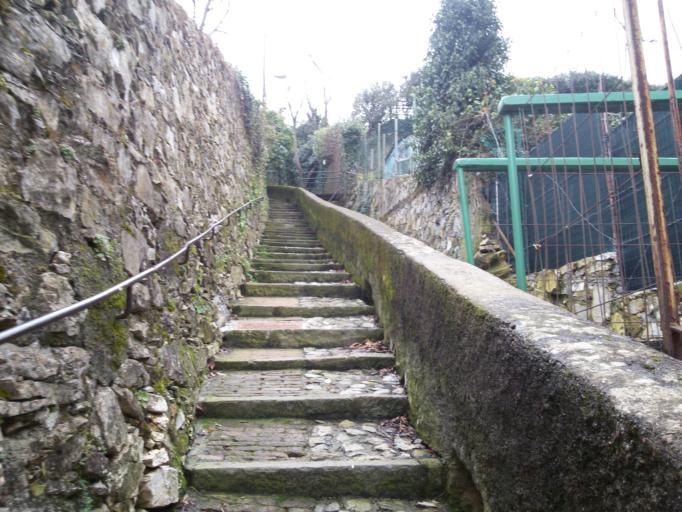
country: IT
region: Liguria
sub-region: Provincia di Genova
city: Genoa
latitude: 44.4186
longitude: 8.9676
